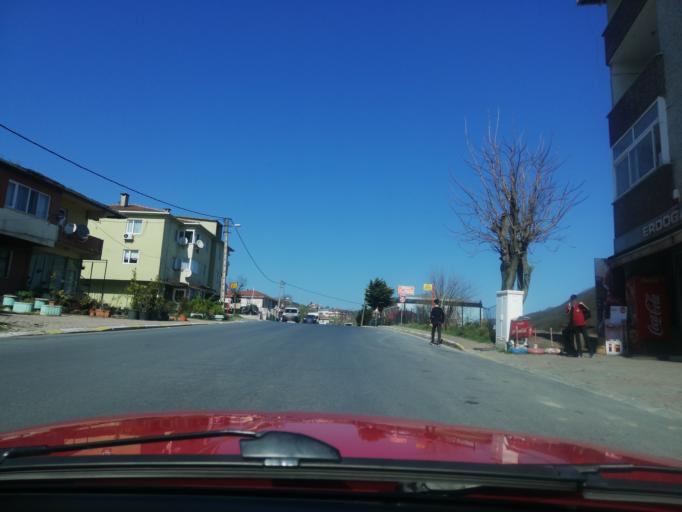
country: TR
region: Istanbul
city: Mahmut Sevket Pasa
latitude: 41.0935
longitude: 29.1430
